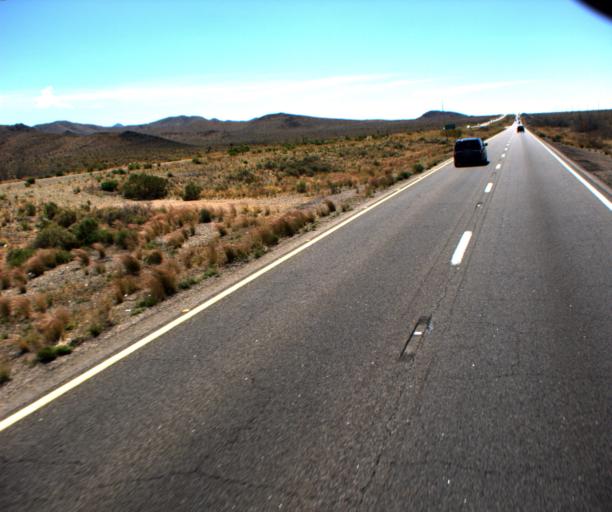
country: US
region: Arizona
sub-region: Mohave County
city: Dolan Springs
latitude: 35.4598
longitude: -114.3044
